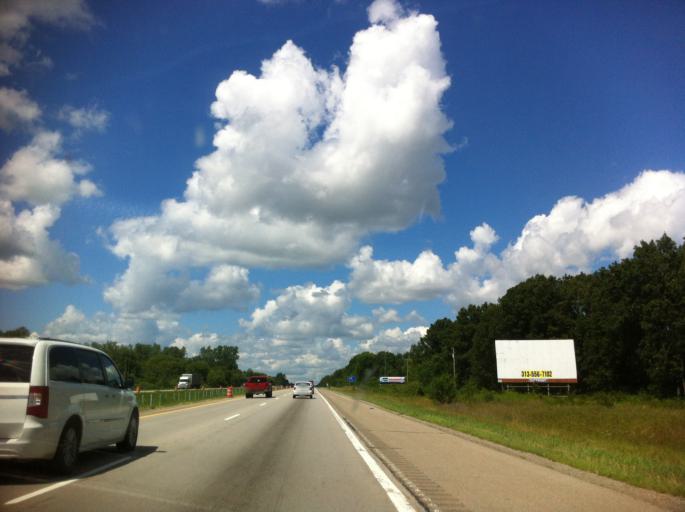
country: US
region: Michigan
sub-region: Washtenaw County
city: Milan
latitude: 42.1384
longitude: -83.6832
